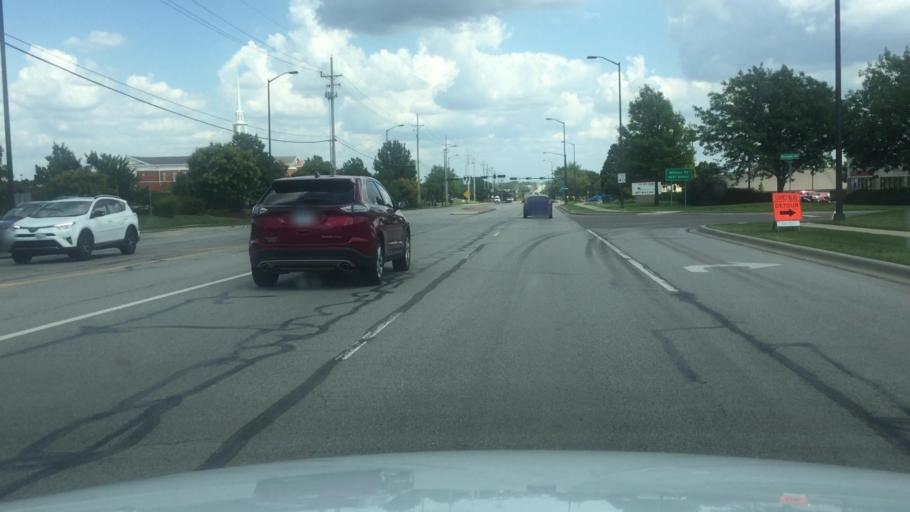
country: US
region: Kansas
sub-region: Johnson County
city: Lenexa
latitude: 38.9710
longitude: -94.7680
